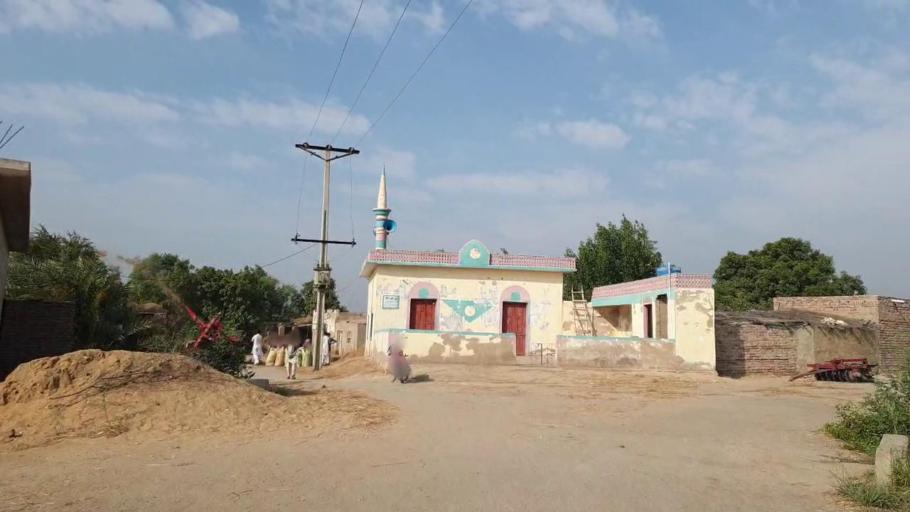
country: PK
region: Sindh
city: Tando Muhammad Khan
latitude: 25.0515
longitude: 68.4339
